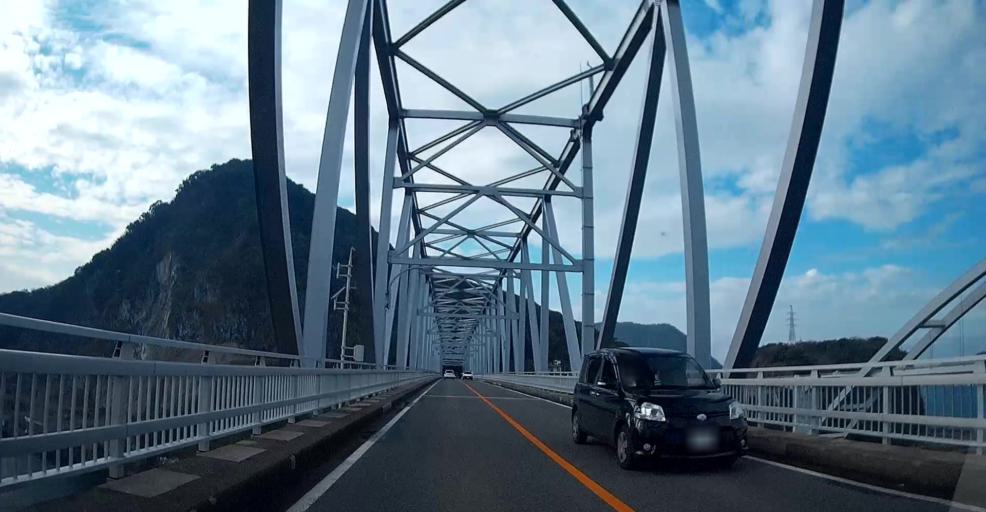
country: JP
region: Kumamoto
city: Yatsushiro
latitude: 32.6111
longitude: 130.4587
